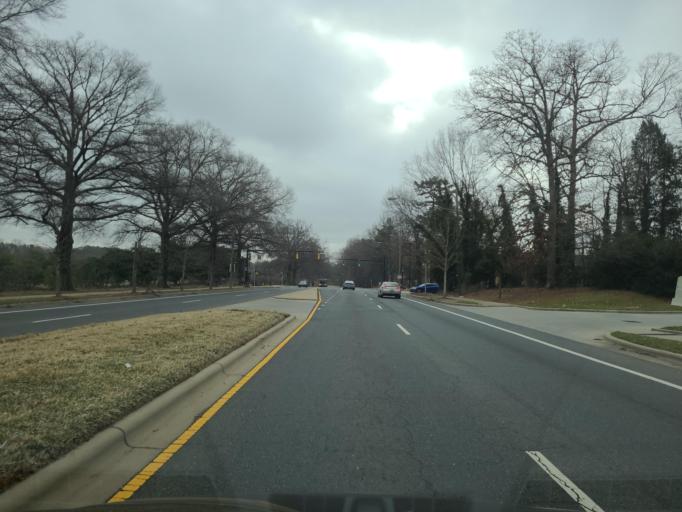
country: US
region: North Carolina
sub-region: Mecklenburg County
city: Matthews
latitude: 35.2059
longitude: -80.7511
